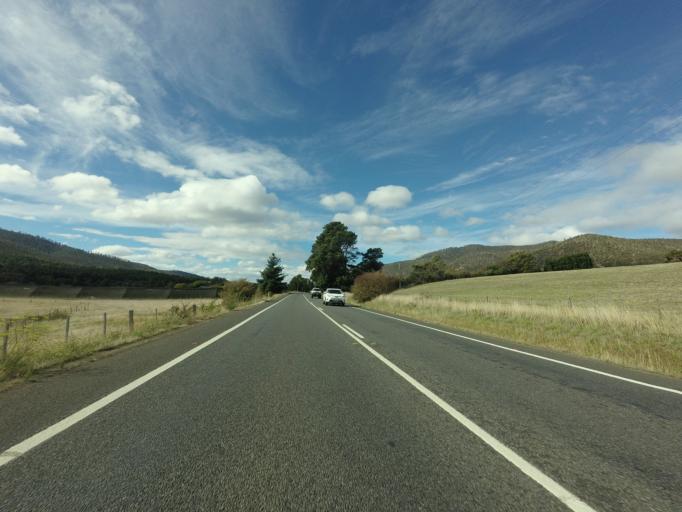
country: AU
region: Tasmania
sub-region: Derwent Valley
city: New Norfolk
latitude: -42.7744
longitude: 147.1201
